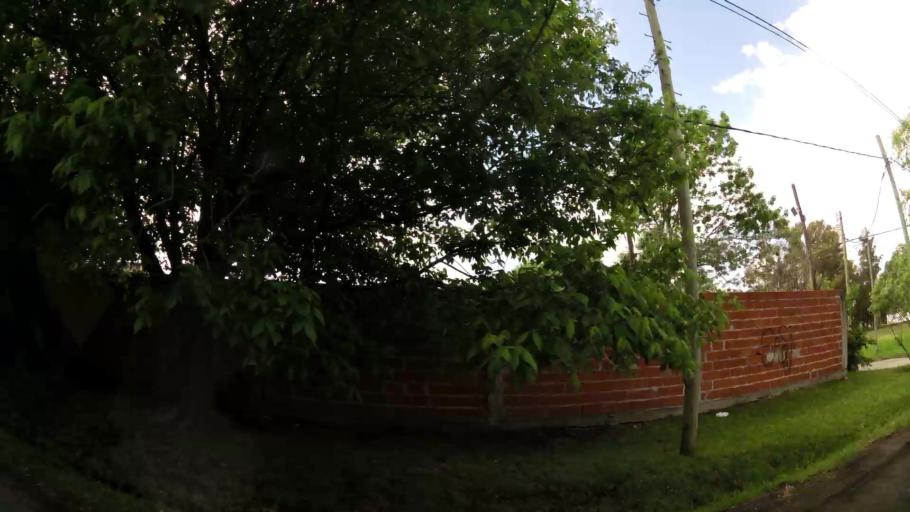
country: AR
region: Buenos Aires
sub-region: Partido de Quilmes
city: Quilmes
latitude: -34.8357
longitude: -58.1892
